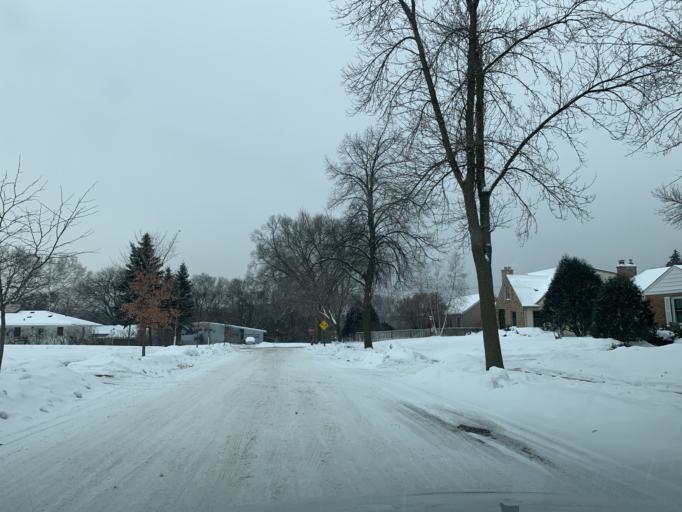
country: US
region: Minnesota
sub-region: Hennepin County
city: Saint Louis Park
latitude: 44.9331
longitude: -93.3316
